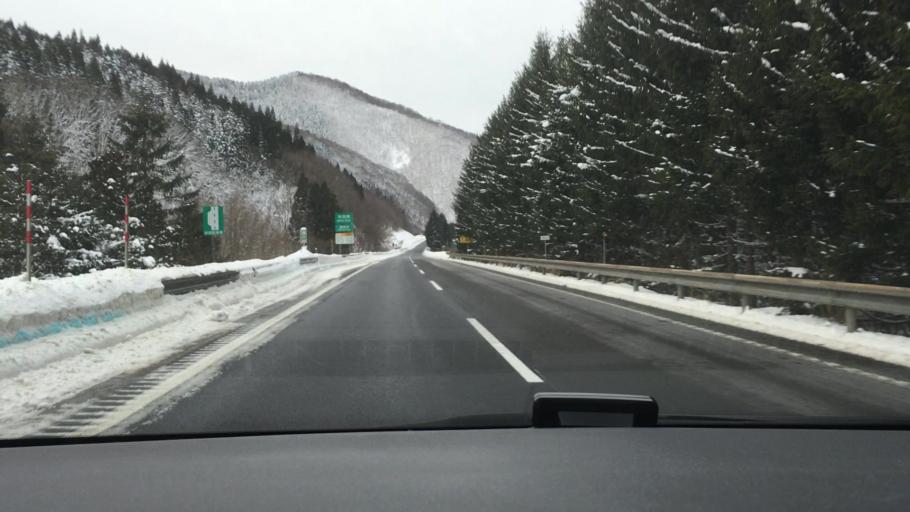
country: JP
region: Akita
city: Hanawa
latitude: 40.1148
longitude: 140.8825
